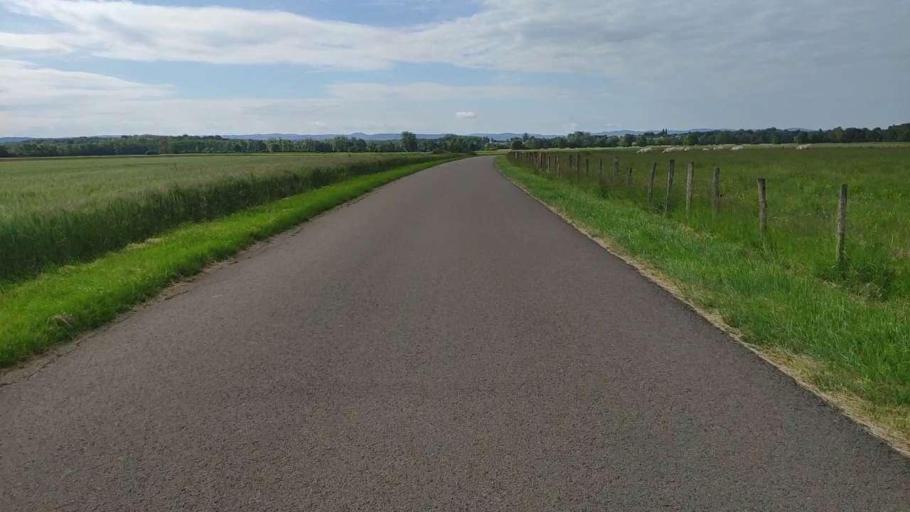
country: FR
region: Franche-Comte
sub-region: Departement du Jura
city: Bletterans
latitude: 46.7308
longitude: 5.4633
